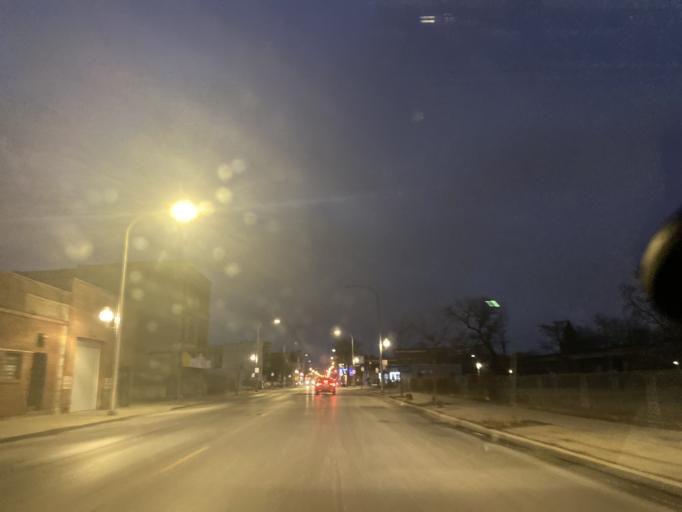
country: US
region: Illinois
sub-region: Cook County
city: Chicago
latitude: 41.7796
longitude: -87.6530
